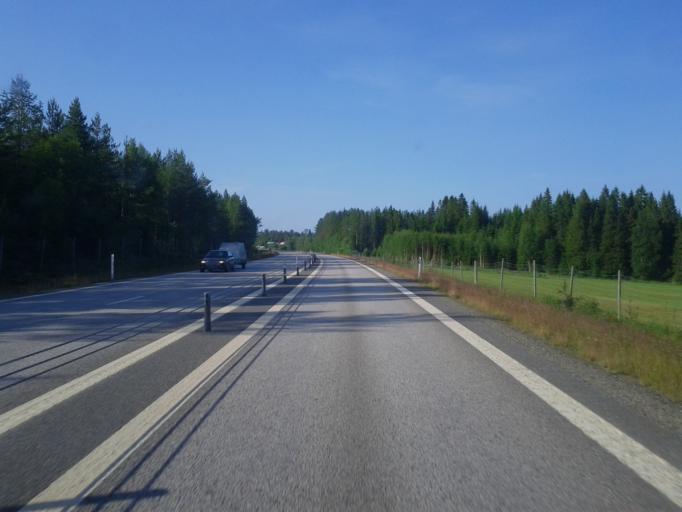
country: SE
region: Vaesterbotten
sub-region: Robertsfors Kommun
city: Robertsfors
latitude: 64.1107
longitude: 20.8788
